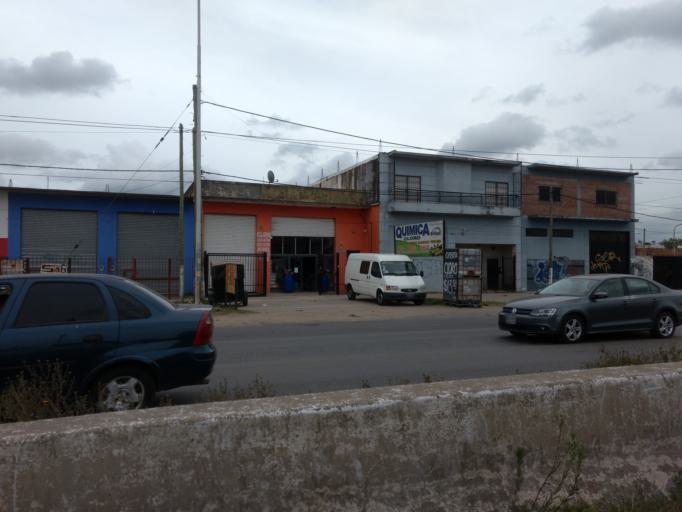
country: AR
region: Buenos Aires
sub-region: Partido de Lomas de Zamora
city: Lomas de Zamora
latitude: -34.7583
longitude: -58.4828
